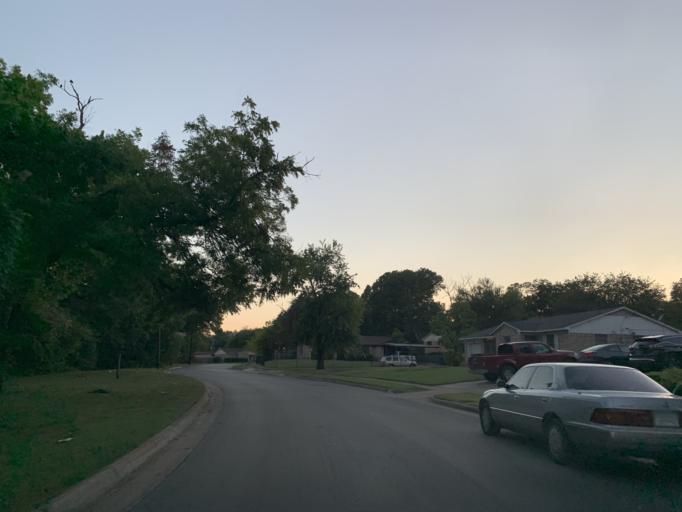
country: US
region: Texas
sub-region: Dallas County
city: Lancaster
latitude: 32.6693
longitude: -96.8011
